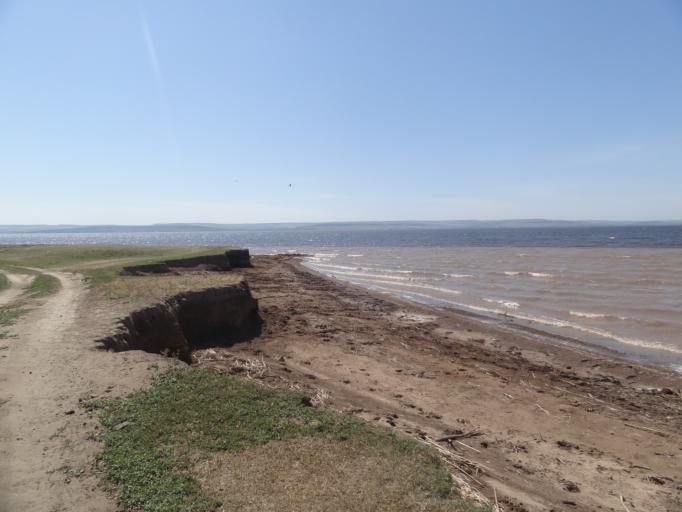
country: RU
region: Saratov
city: Krasnoarmeysk
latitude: 51.1600
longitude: 45.9017
